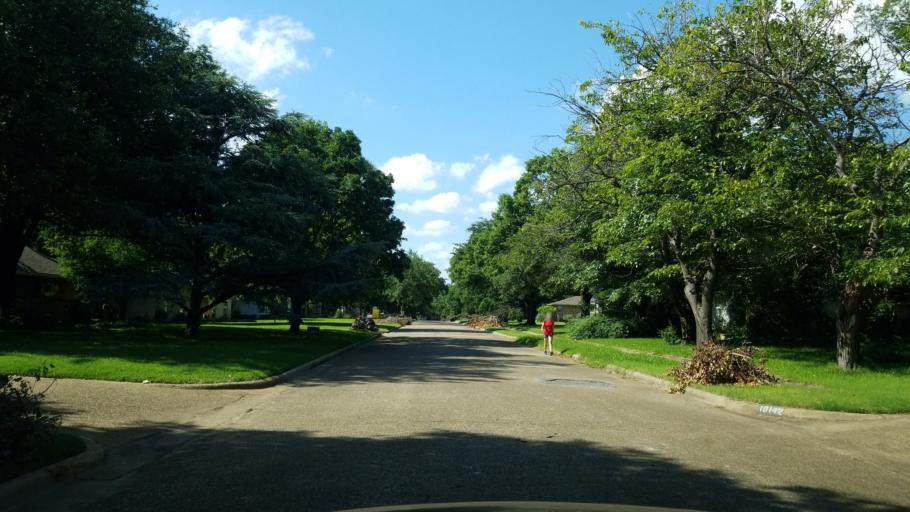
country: US
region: Texas
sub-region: Dallas County
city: University Park
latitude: 32.8844
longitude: -96.8487
